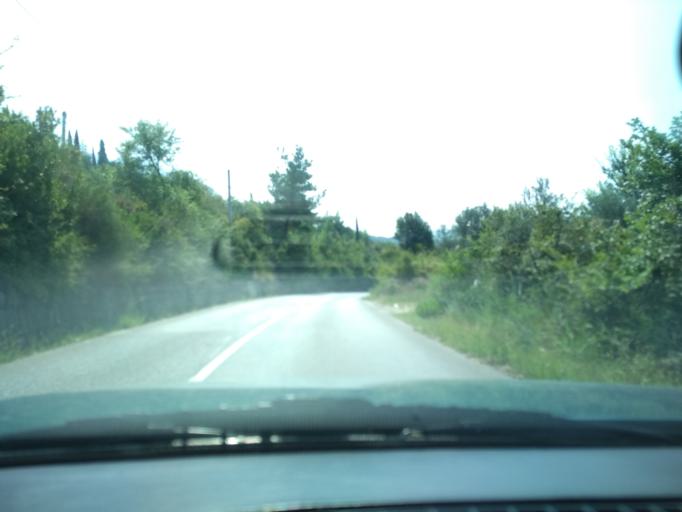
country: ME
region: Kotor
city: Kotor
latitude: 42.3897
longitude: 18.7575
